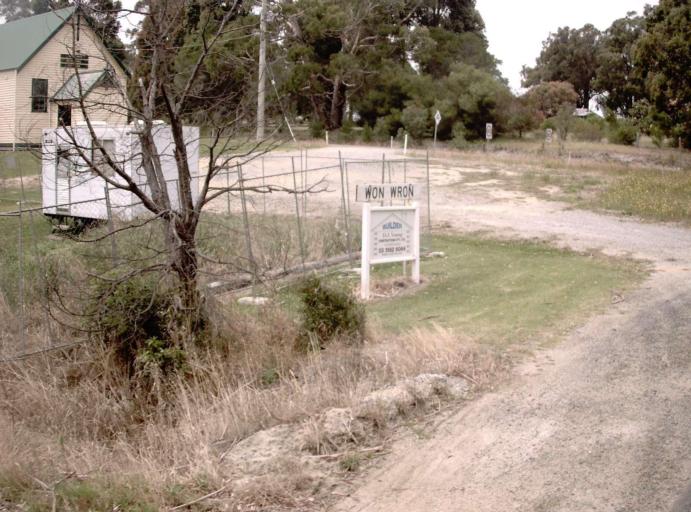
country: AU
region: Victoria
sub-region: Latrobe
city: Traralgon
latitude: -38.4729
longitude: 146.7171
